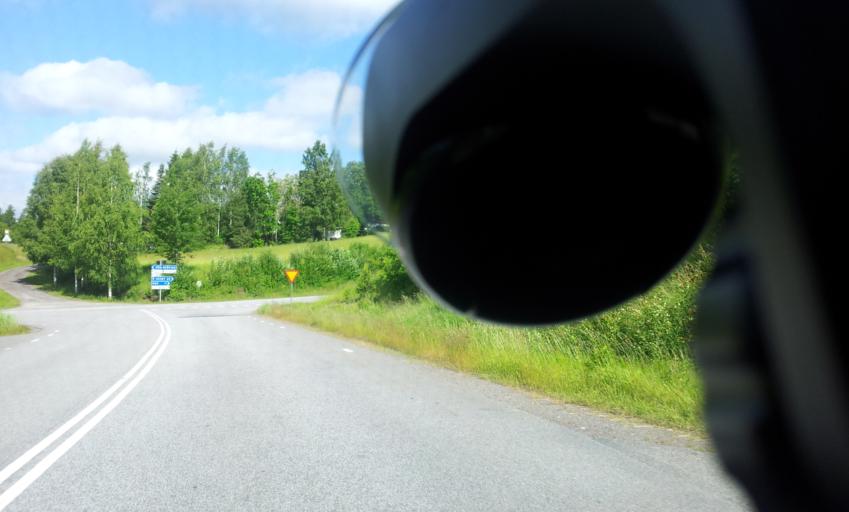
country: SE
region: OEstergoetland
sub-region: Soderkopings Kommun
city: Soederkoeping
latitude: 58.4927
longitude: 16.3084
